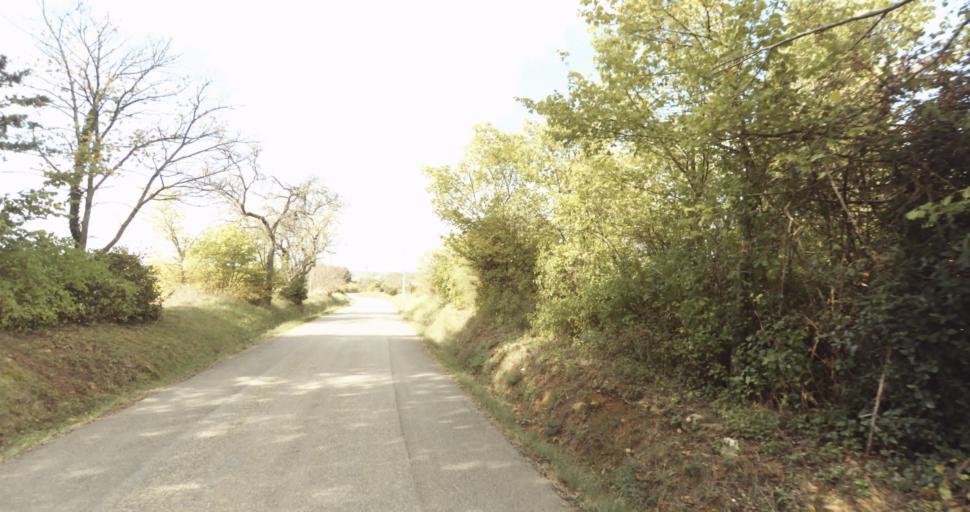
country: FR
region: Provence-Alpes-Cote d'Azur
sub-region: Departement des Bouches-du-Rhone
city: Venelles
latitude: 43.5770
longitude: 5.4833
